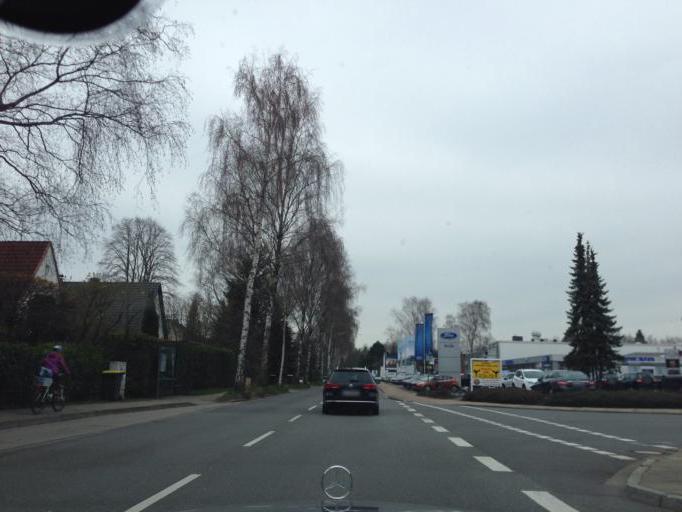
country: DE
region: Hamburg
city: Sasel
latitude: 53.6422
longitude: 10.1272
